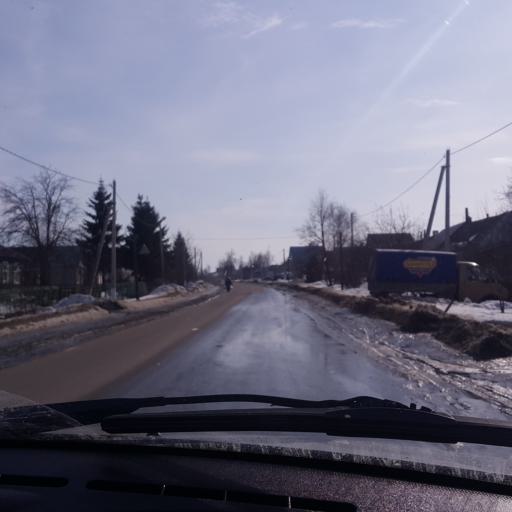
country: RU
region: Tambov
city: Sosnovka
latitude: 53.2379
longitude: 41.3651
